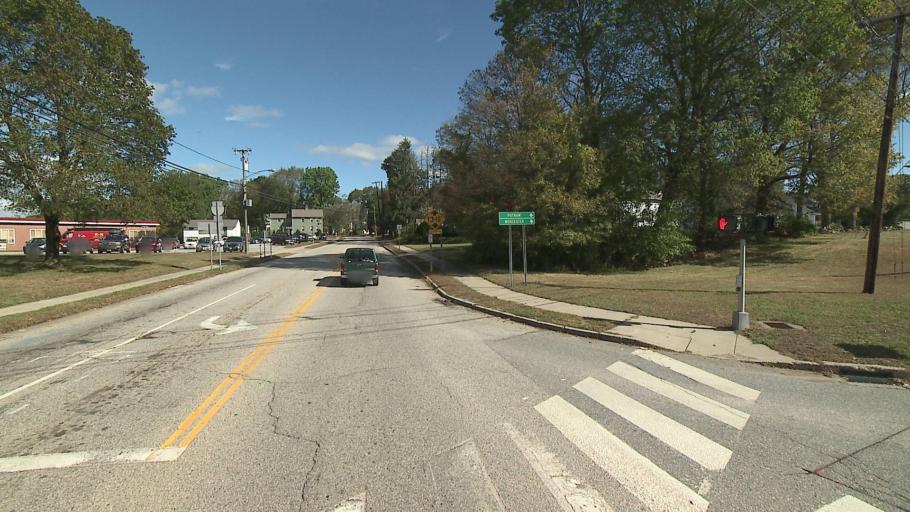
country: US
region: Connecticut
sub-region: Windham County
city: Danielson
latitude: 41.8095
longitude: -71.8788
